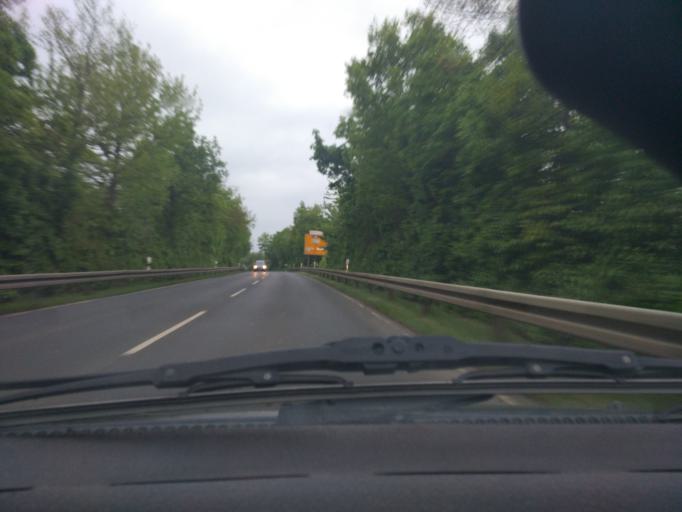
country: DE
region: Hesse
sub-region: Regierungsbezirk Darmstadt
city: Rudesheim am Rhein
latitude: 49.9600
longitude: 7.9424
